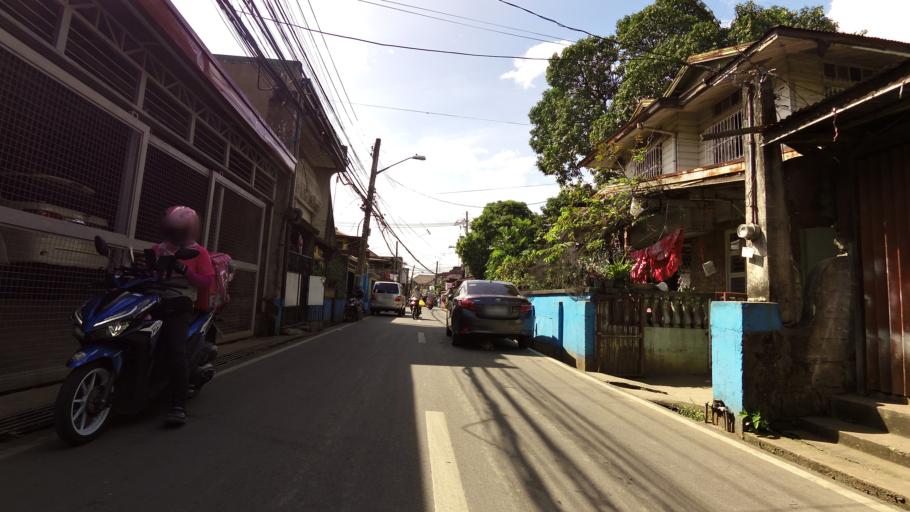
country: PH
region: Calabarzon
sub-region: Province of Rizal
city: Cainta
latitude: 14.5695
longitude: 121.1287
